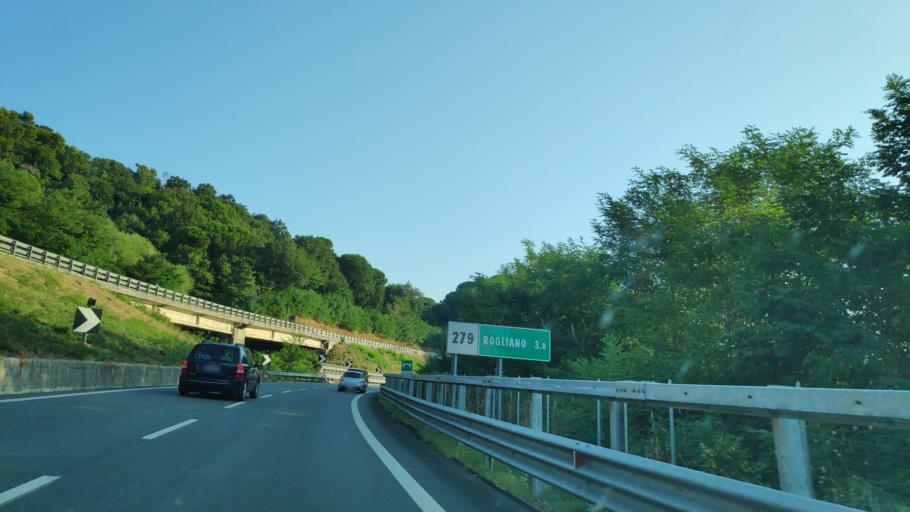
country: IT
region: Calabria
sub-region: Provincia di Cosenza
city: Belsito
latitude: 39.1698
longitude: 16.2927
